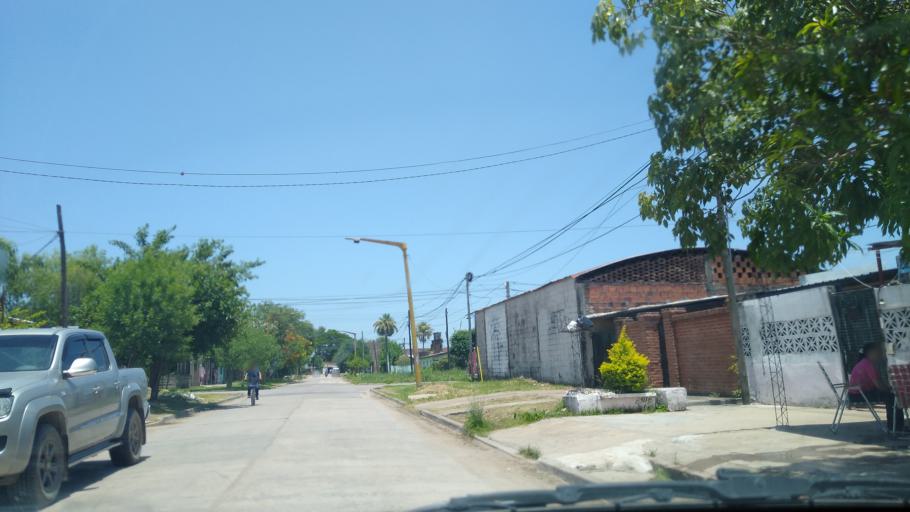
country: AR
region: Chaco
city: Barranqueras
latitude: -27.4896
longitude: -58.9401
